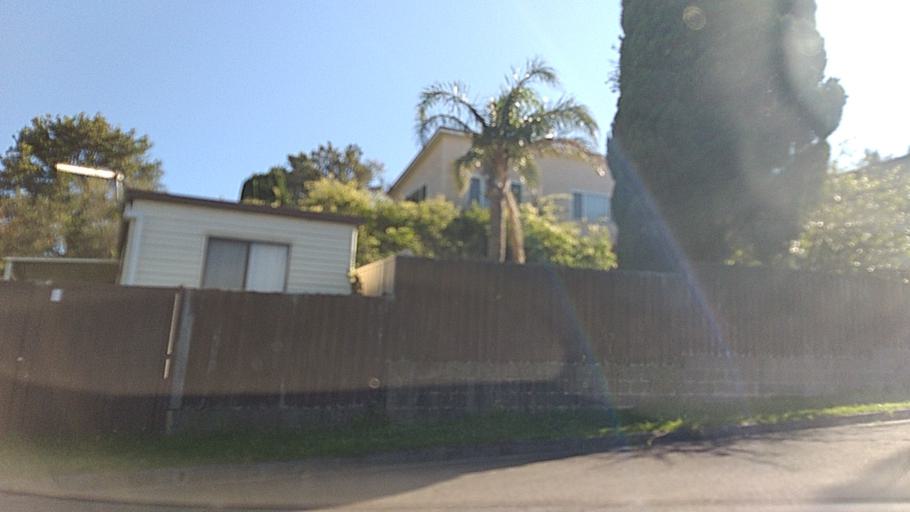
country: AU
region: New South Wales
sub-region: Wollongong
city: Corrimal
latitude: -34.3678
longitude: 150.8926
